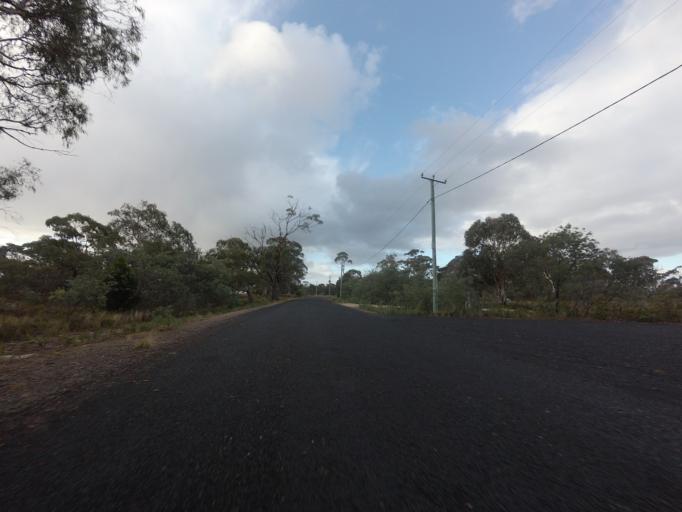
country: AU
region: Tasmania
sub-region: Break O'Day
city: St Helens
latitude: -42.1059
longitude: 148.0756
